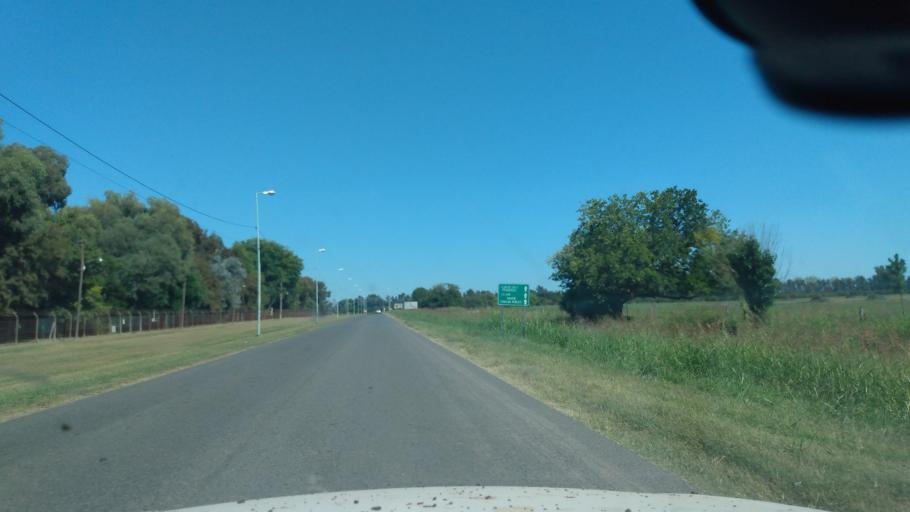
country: AR
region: Buenos Aires
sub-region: Partido de Lujan
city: Lujan
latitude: -34.5096
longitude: -59.0874
